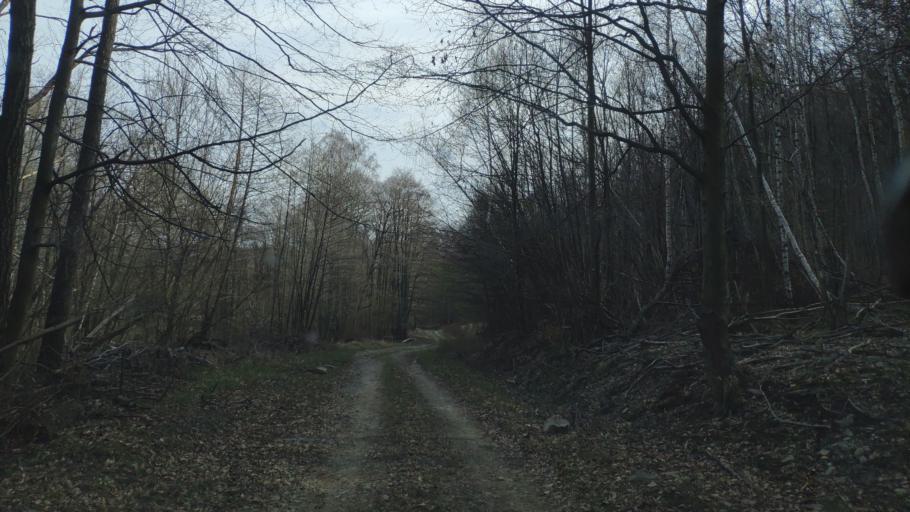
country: SK
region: Kosicky
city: Moldava nad Bodvou
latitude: 48.7398
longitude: 21.0544
